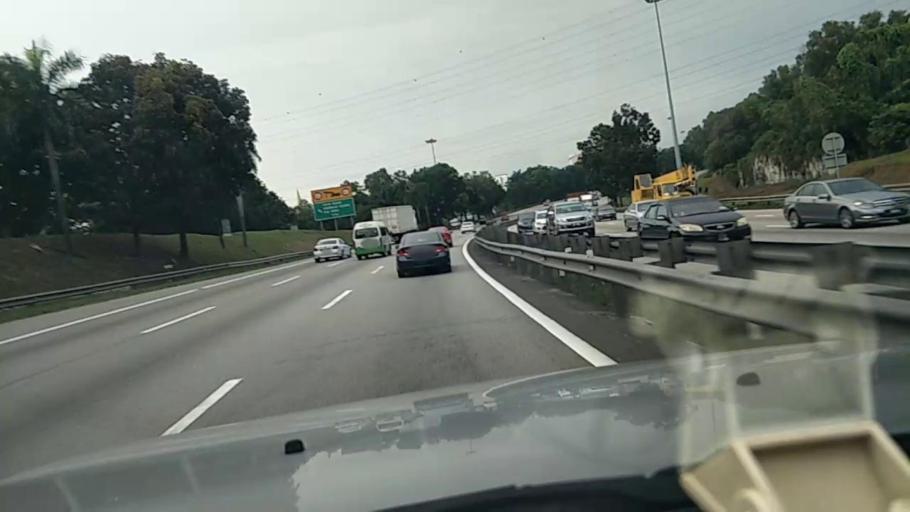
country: MY
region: Selangor
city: Subang Jaya
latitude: 3.0575
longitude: 101.5590
